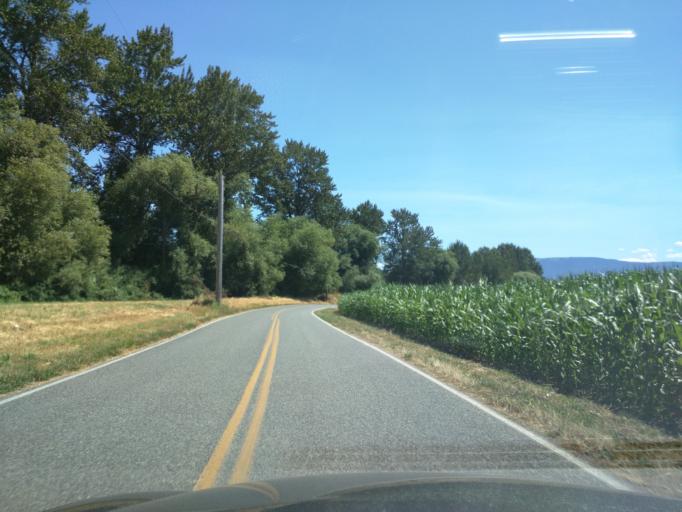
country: US
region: Washington
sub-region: Whatcom County
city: Lynden
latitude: 48.9276
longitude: -122.4013
